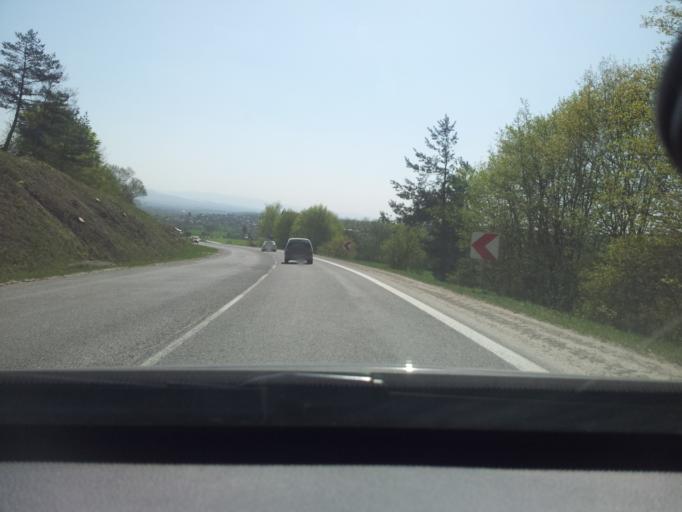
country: SK
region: Trenciansky
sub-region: Okres Trencin
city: Trencin
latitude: 48.8088
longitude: 18.0932
